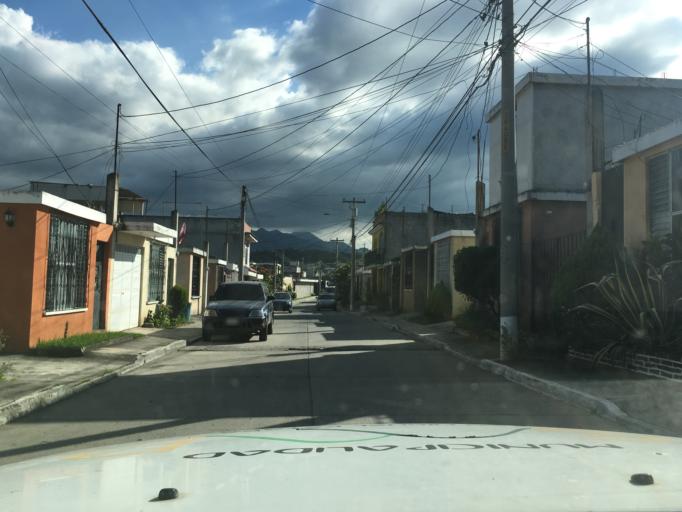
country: GT
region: Guatemala
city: Petapa
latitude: 14.5007
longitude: -90.5665
